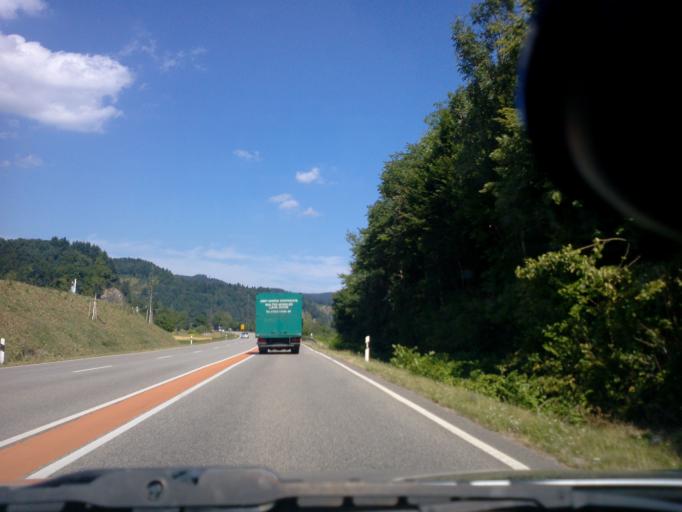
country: DE
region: Baden-Wuerttemberg
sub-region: Freiburg Region
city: Biberach
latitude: 48.3288
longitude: 8.0287
